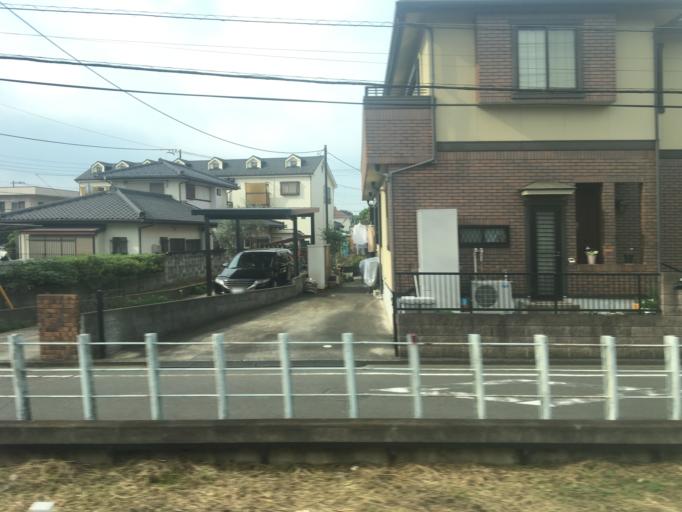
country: JP
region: Saitama
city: Sayama
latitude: 35.8349
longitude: 139.4247
